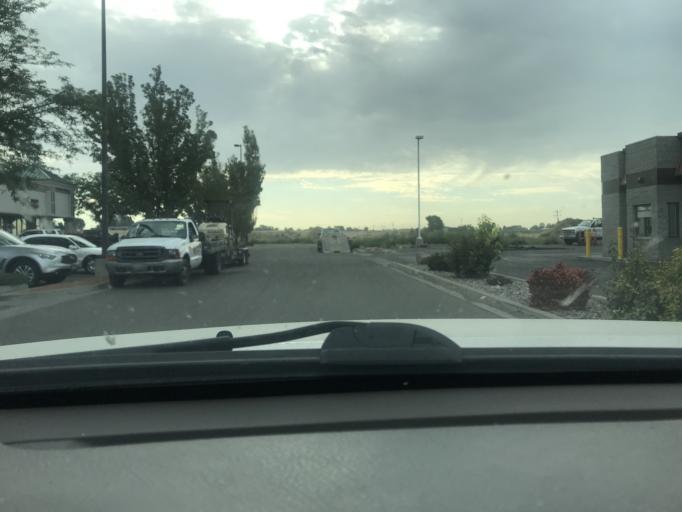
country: US
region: Idaho
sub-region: Jerome County
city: Jerome
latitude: 42.6922
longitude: -114.5177
